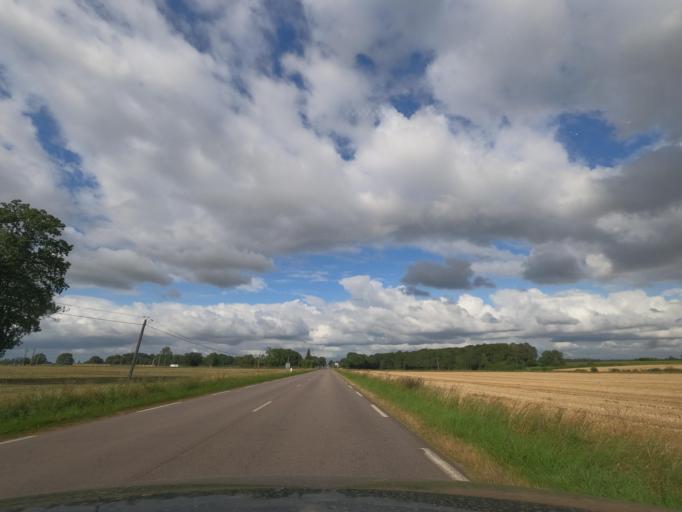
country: FR
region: Haute-Normandie
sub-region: Departement de l'Eure
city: Broglie
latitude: 48.9745
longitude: 0.4861
